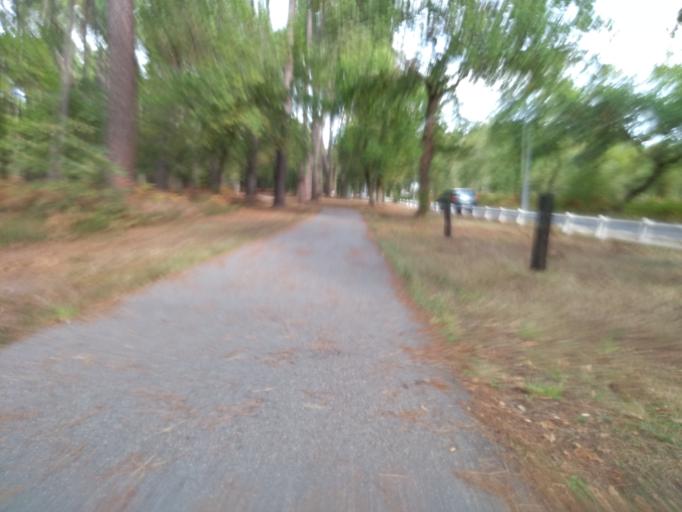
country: FR
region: Aquitaine
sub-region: Departement de la Gironde
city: Canejan
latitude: 44.7540
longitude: -0.6519
